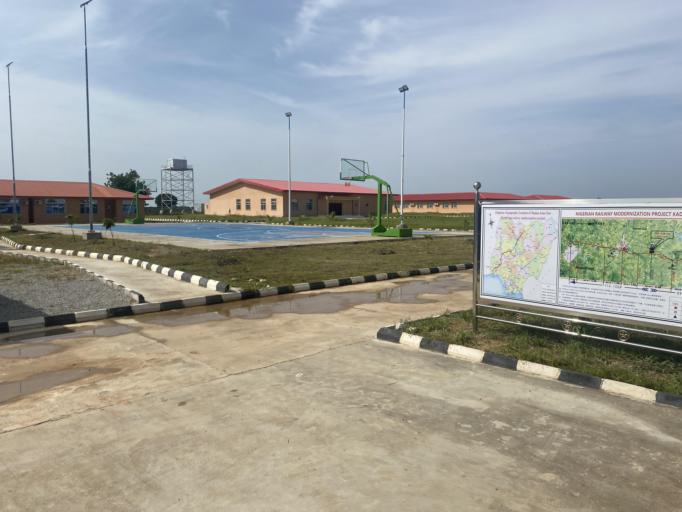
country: NG
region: Kano
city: Kumbotso
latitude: 11.9034
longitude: 8.4414
